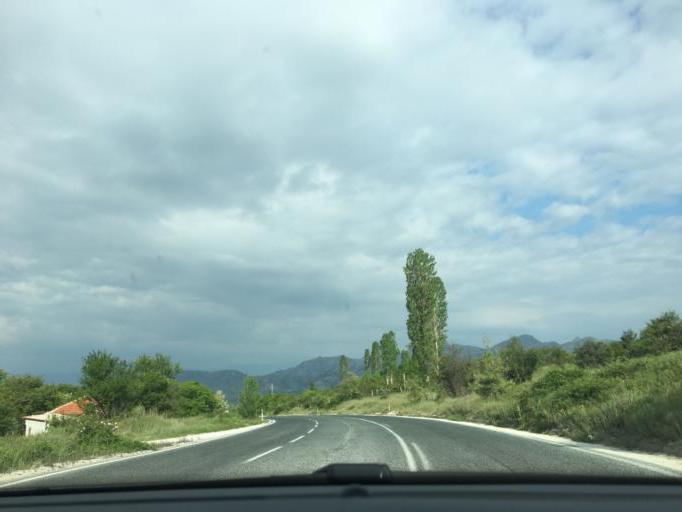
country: MK
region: Prilep
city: Prilep
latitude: 41.3685
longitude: 21.6410
